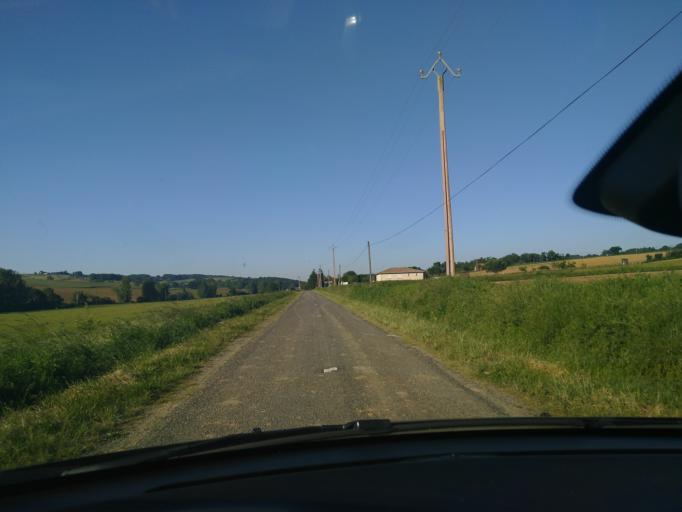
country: FR
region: Midi-Pyrenees
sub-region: Departement du Tarn-et-Garonne
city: Beaumont-de-Lomagne
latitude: 43.8151
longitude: 1.0401
